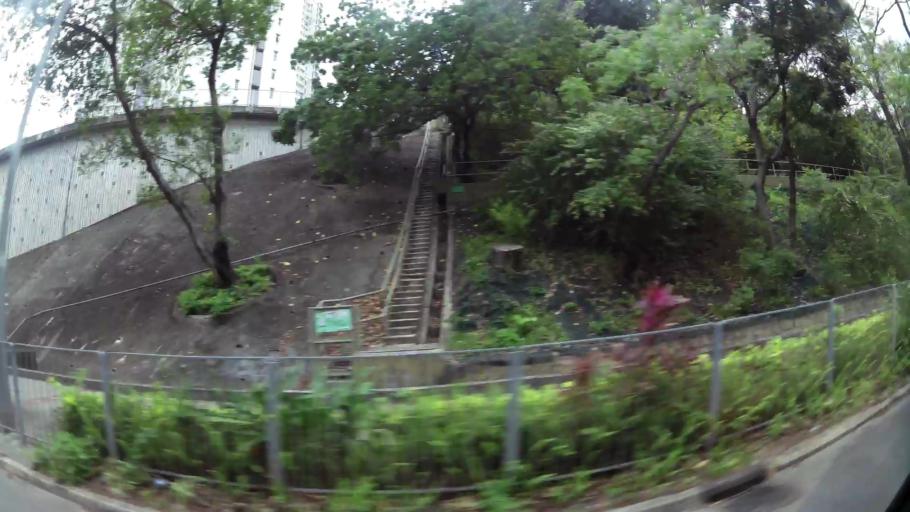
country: HK
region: Wong Tai Sin
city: Wong Tai Sin
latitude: 22.3343
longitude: 114.1908
